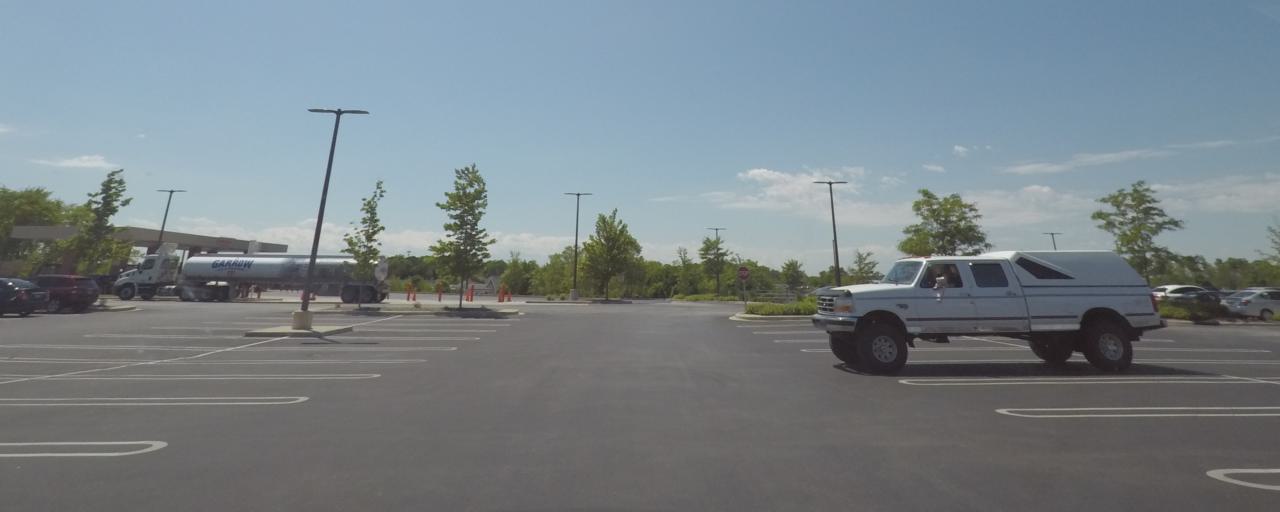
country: US
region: Wisconsin
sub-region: Waukesha County
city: New Berlin
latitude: 42.9454
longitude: -88.1066
